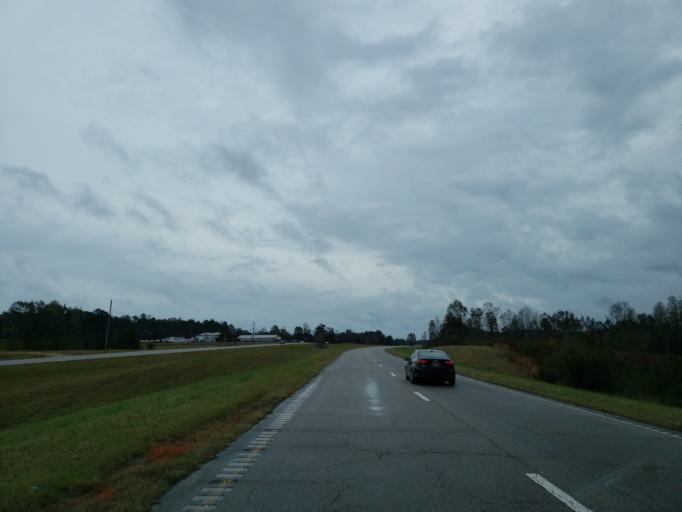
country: US
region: Mississippi
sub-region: Jones County
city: Sharon
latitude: 31.7031
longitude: -88.9129
